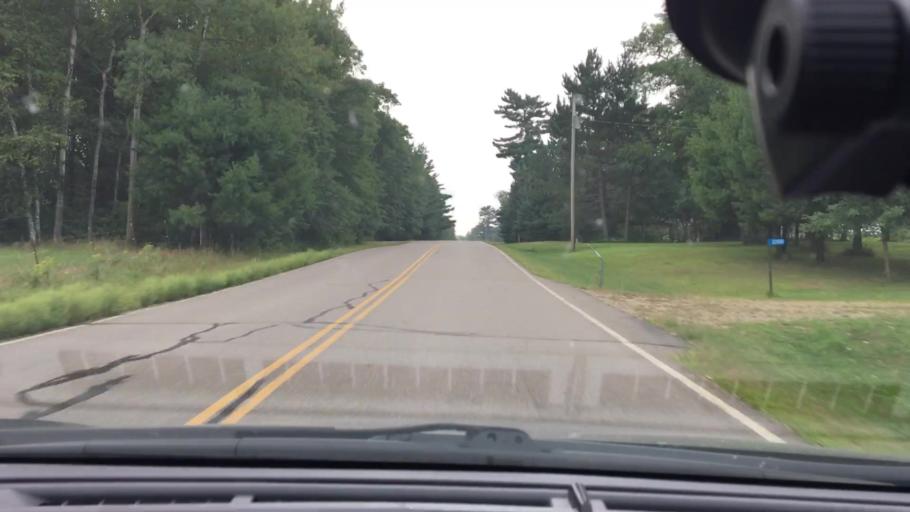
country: US
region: Minnesota
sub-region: Crow Wing County
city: Cross Lake
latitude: 46.6427
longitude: -94.0096
